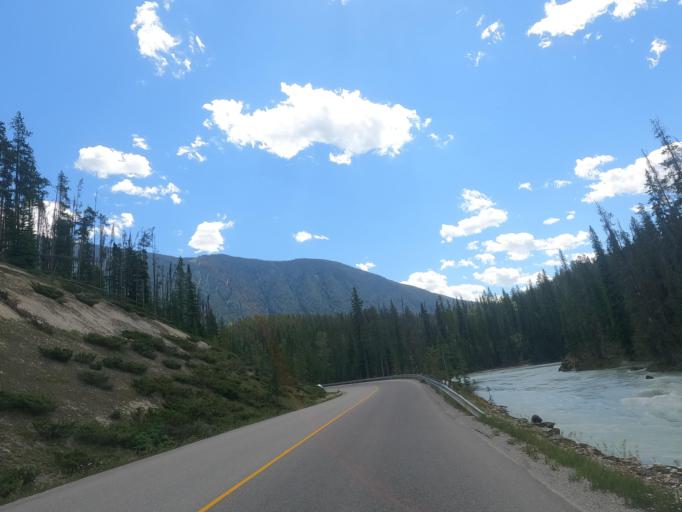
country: CA
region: Alberta
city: Lake Louise
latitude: 51.3825
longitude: -116.5270
